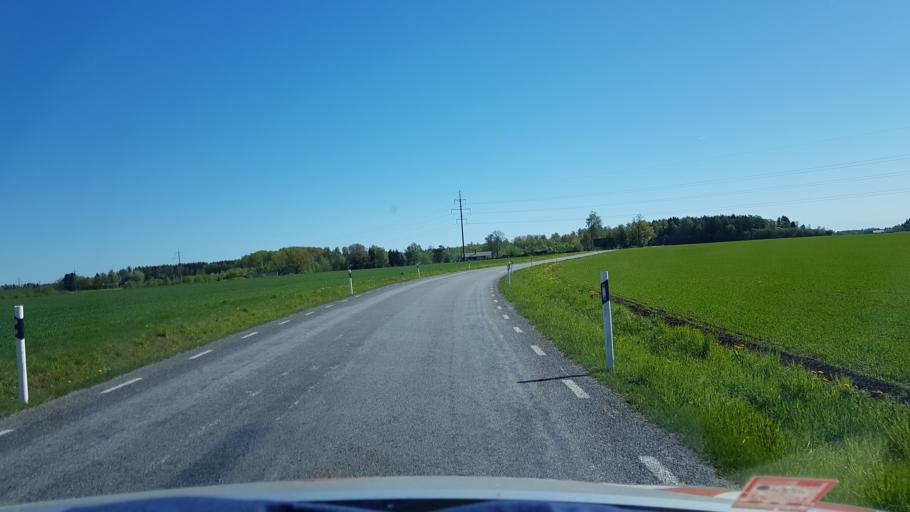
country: EE
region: Tartu
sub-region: Tartu linn
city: Tartu
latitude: 58.4003
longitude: 26.8696
